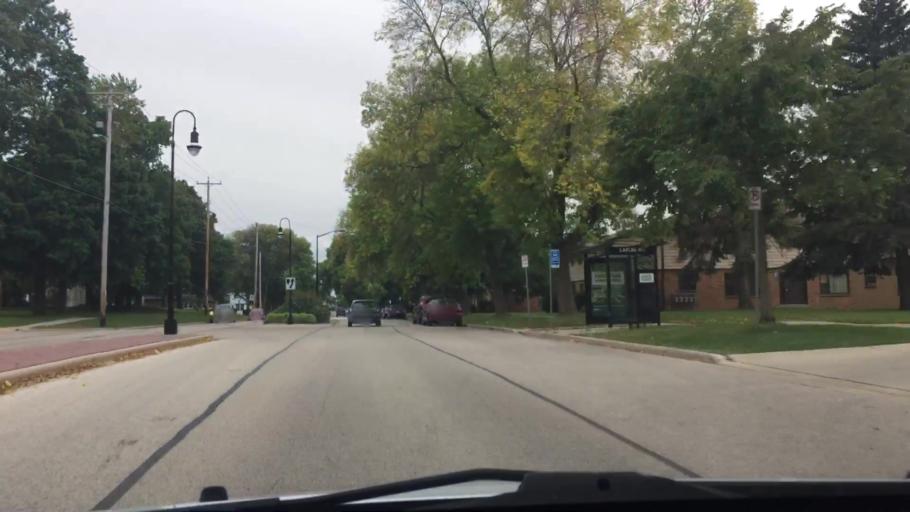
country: US
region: Wisconsin
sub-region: Waukesha County
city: Waukesha
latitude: 43.0011
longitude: -88.2320
